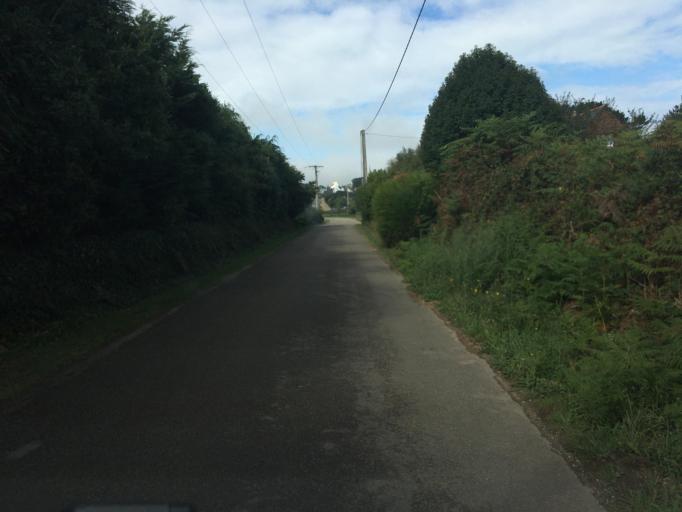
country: FR
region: Brittany
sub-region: Departement du Finistere
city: Beuzec-Cap-Sizun
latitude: 48.0751
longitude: -4.5007
